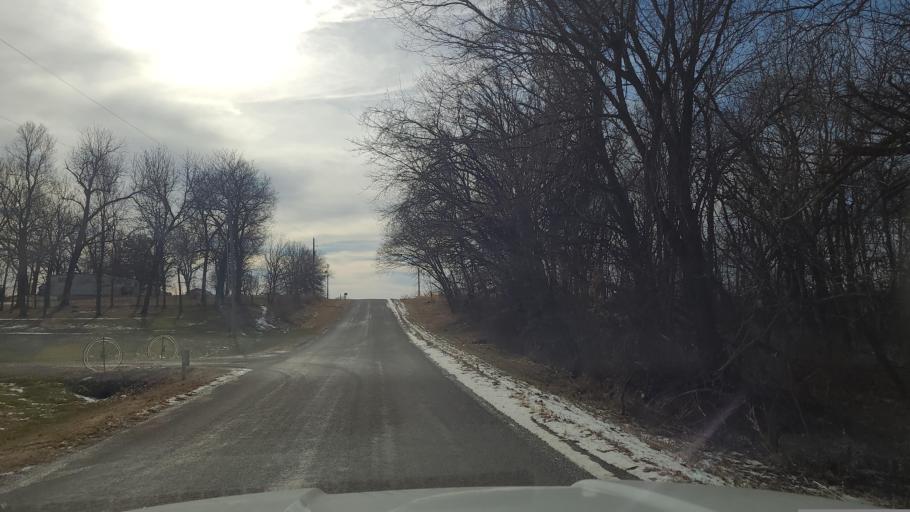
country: US
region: Kansas
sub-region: Douglas County
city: Lawrence
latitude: 38.8925
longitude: -95.1864
